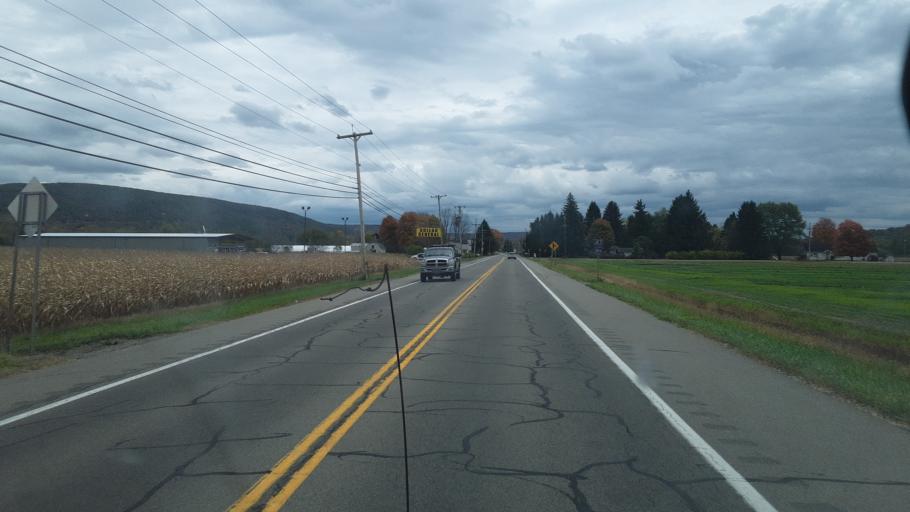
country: US
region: New York
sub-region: Allegany County
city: Belmont
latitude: 42.2102
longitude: -78.0159
